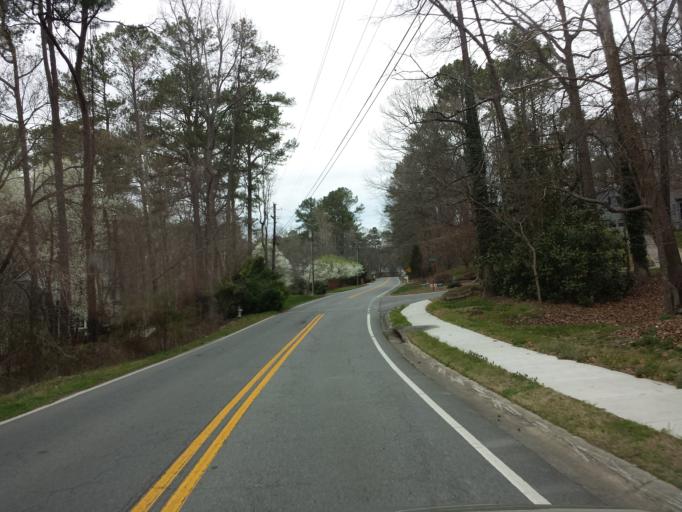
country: US
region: Georgia
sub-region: Cherokee County
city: Woodstock
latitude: 34.0243
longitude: -84.5108
